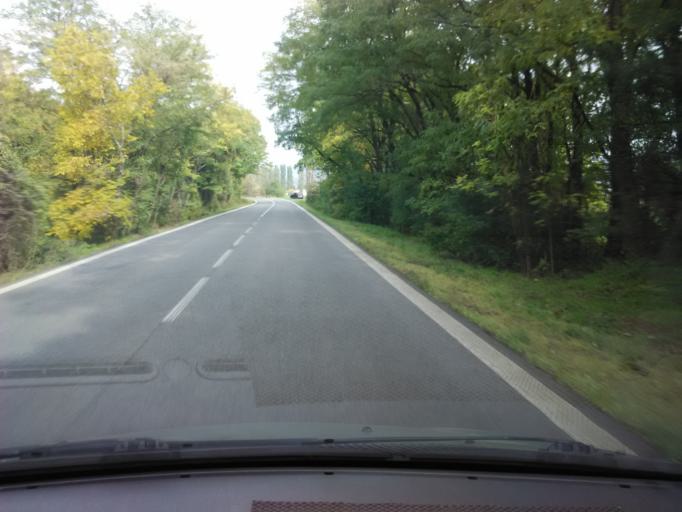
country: SK
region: Nitriansky
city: Tlmace
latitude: 48.2806
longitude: 18.5220
